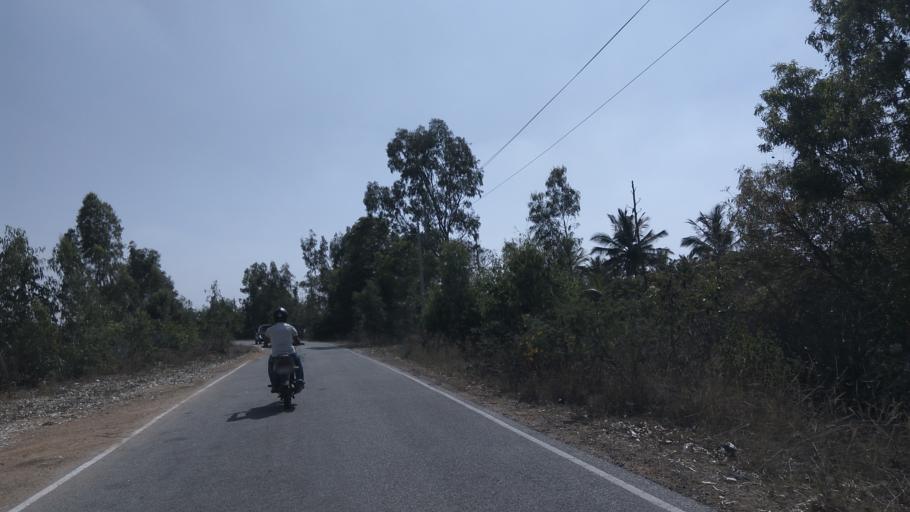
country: IN
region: Karnataka
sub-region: Kolar
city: Mulbagal
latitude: 13.1921
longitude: 78.3540
